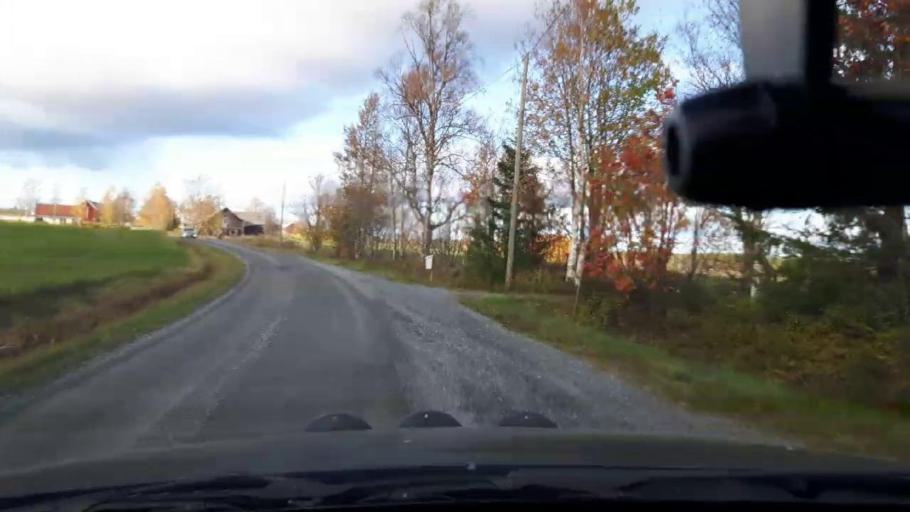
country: SE
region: Jaemtland
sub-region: Bergs Kommun
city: Hoverberg
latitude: 63.0562
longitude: 14.2393
